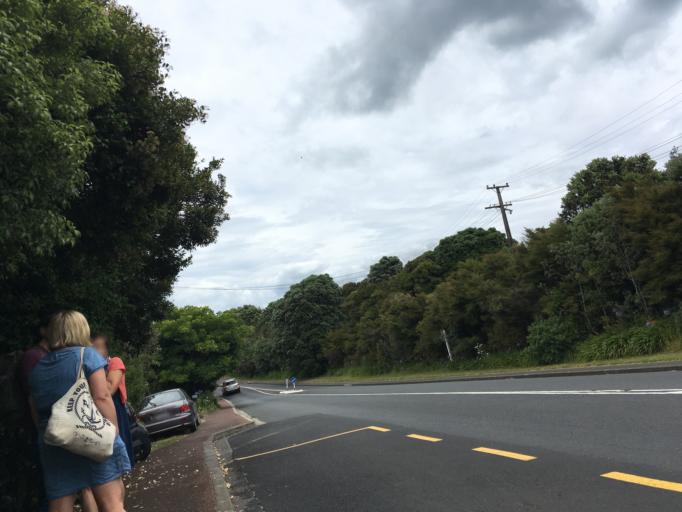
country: NZ
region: Auckland
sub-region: Auckland
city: Pakuranga
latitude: -36.7969
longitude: 175.0325
